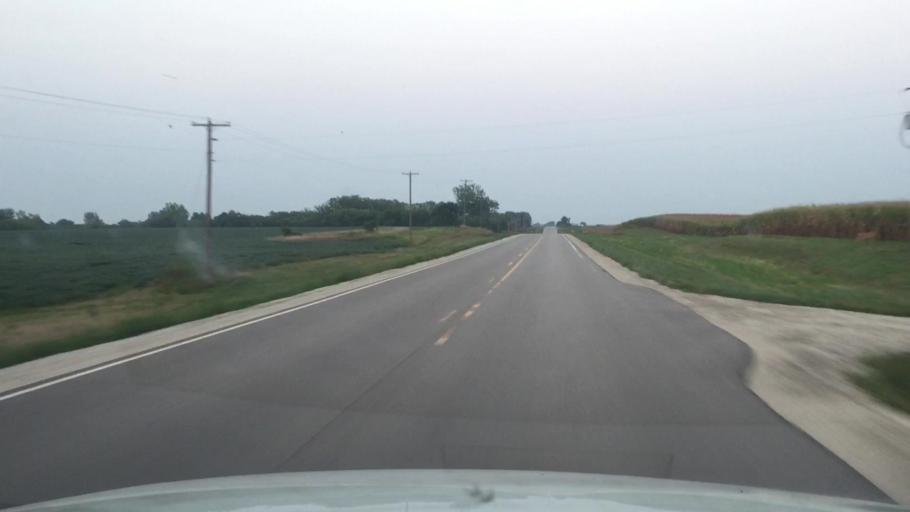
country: US
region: Iowa
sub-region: Warren County
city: Indianola
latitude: 41.1826
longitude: -93.4887
